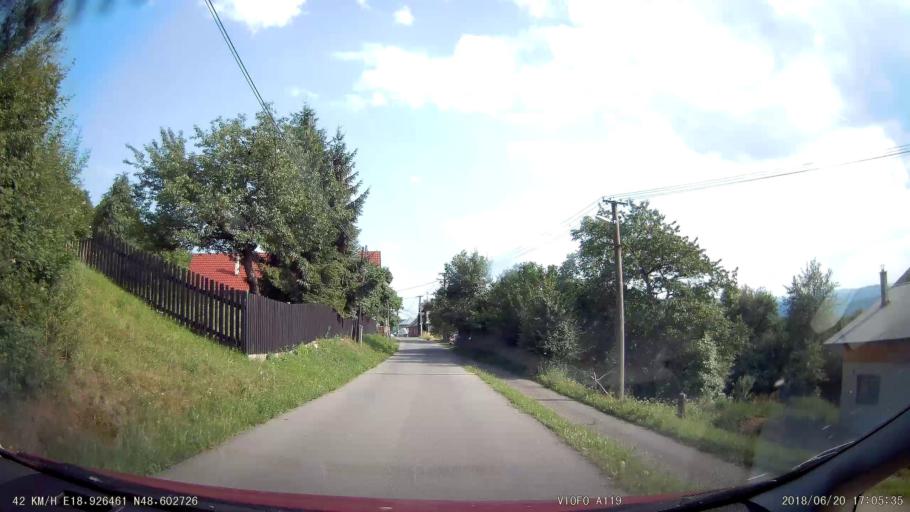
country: SK
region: Banskobystricky
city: Ziar nad Hronom
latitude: 48.6027
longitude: 18.9265
